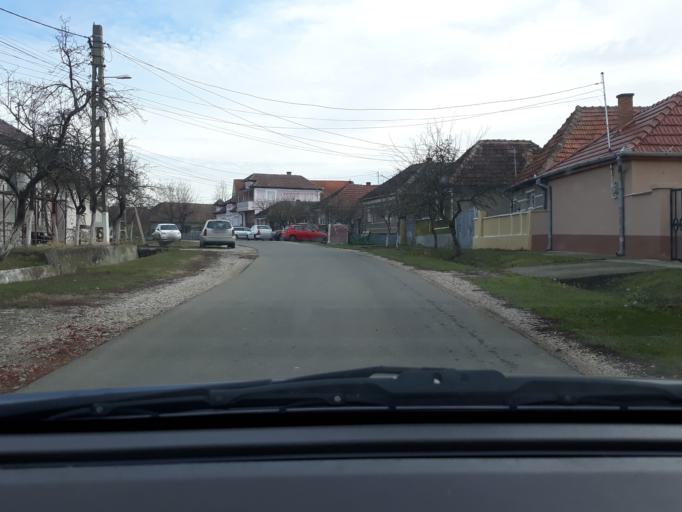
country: RO
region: Bihor
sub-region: Comuna Osorheiu
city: Alparea
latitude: 47.0118
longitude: 22.0216
